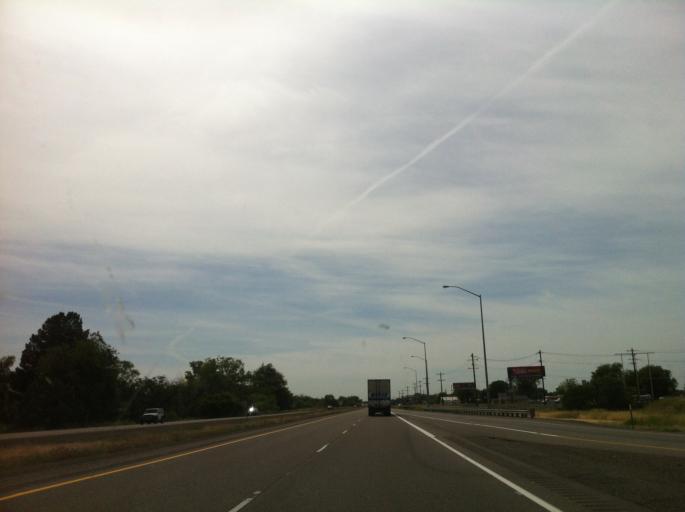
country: US
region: Oregon
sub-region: Malheur County
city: Ontario
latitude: 44.0505
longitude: -116.9790
